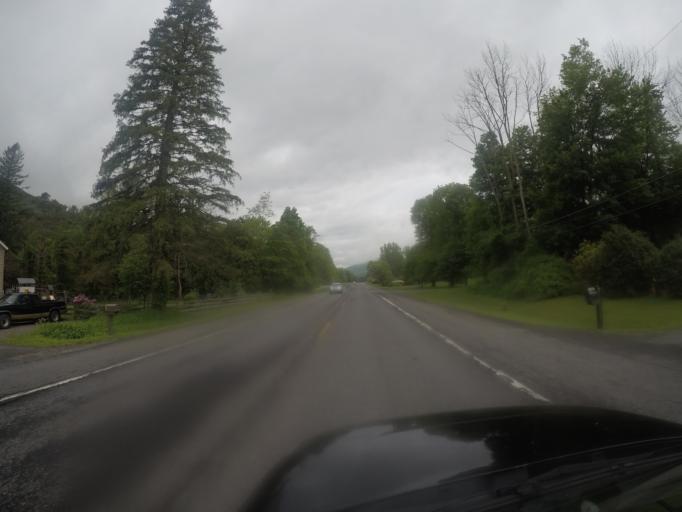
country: US
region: New York
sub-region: Ulster County
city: Shokan
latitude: 42.0301
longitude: -74.2738
